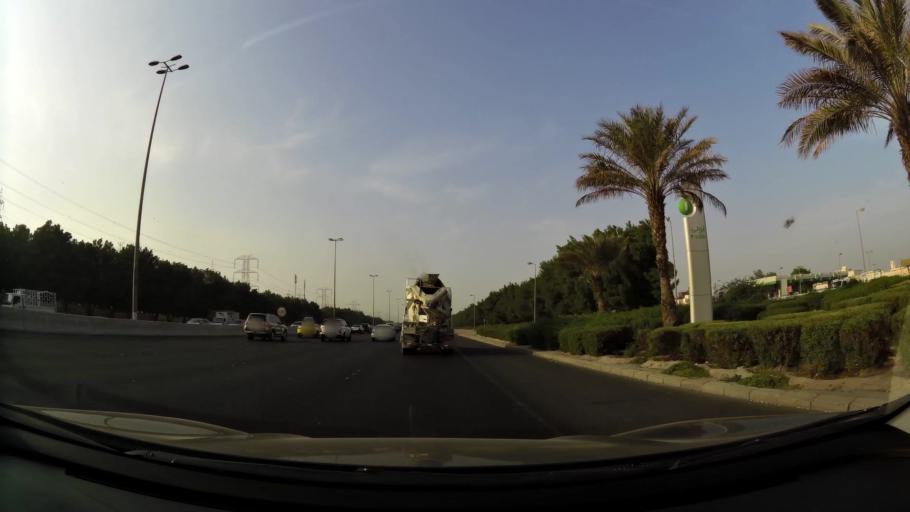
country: KW
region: Mubarak al Kabir
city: Sabah as Salim
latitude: 29.2294
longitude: 48.0531
